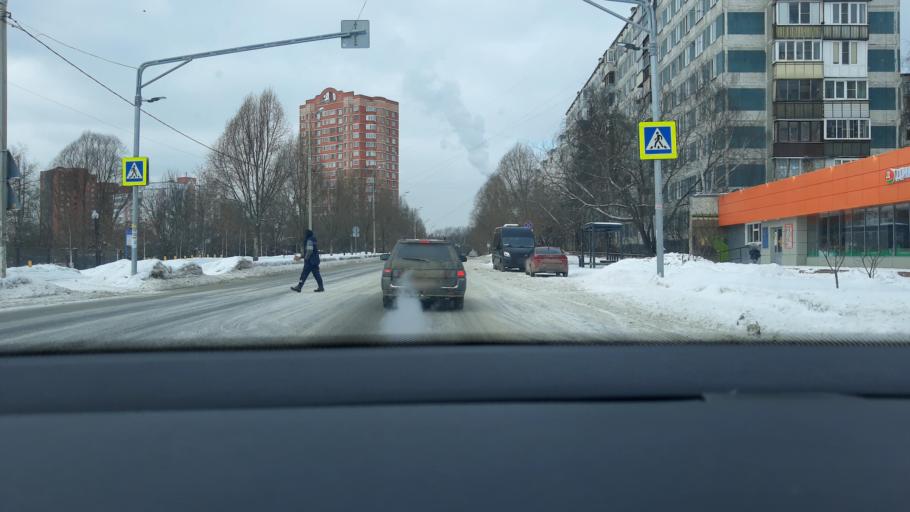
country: RU
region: Moskovskaya
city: Mytishchi
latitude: 55.9106
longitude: 37.7540
